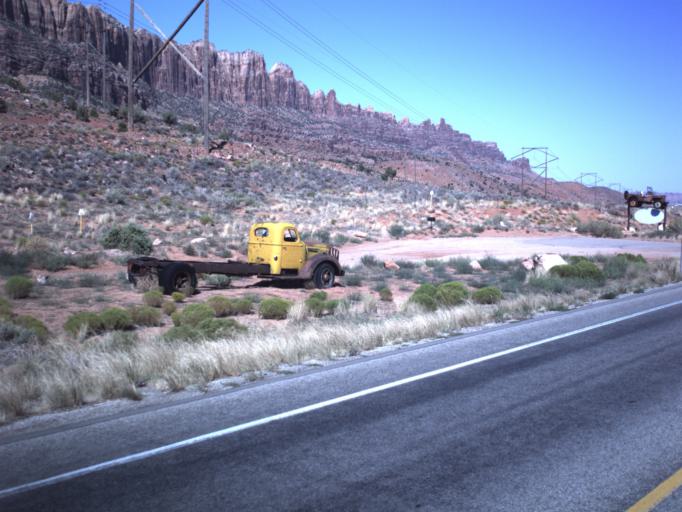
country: US
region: Utah
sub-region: Grand County
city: Moab
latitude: 38.4822
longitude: -109.4593
